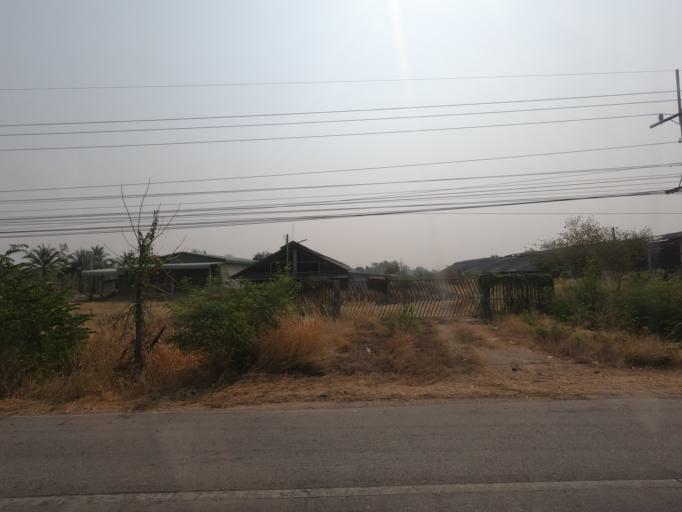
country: TH
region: Khon Kaen
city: Phon
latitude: 15.8571
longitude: 102.6233
